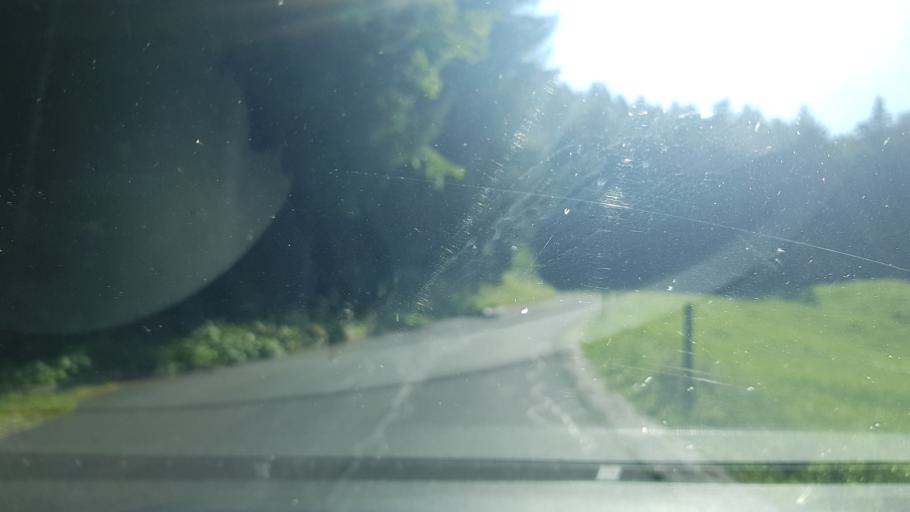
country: SI
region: Ravne na Koroskem
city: Kotlje
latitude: 46.5056
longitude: 14.9599
